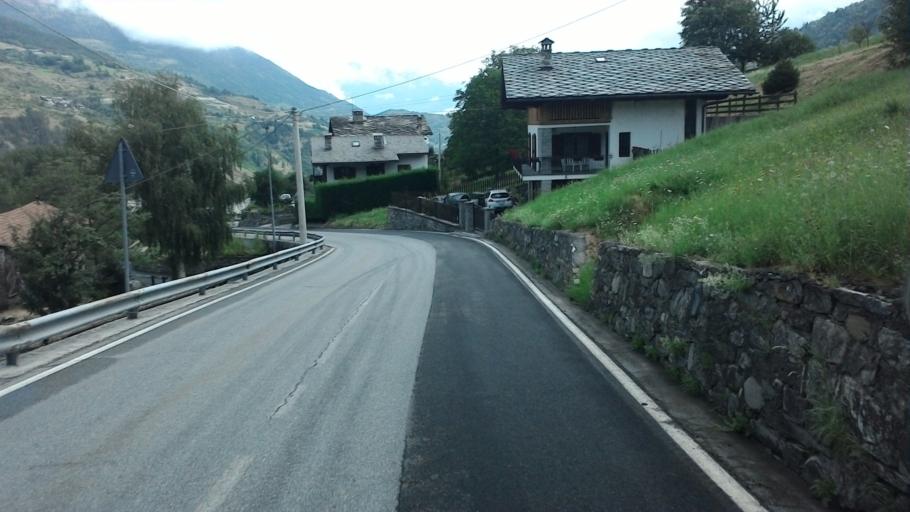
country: IT
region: Aosta Valley
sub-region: Valle d'Aosta
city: Introd
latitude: 45.6958
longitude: 7.1853
